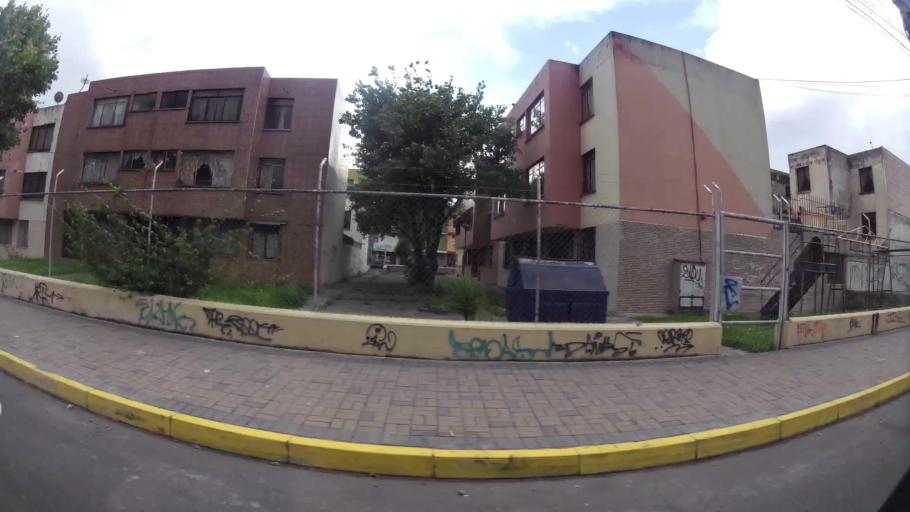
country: EC
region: Pichincha
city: Quito
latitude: -0.2654
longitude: -78.5411
